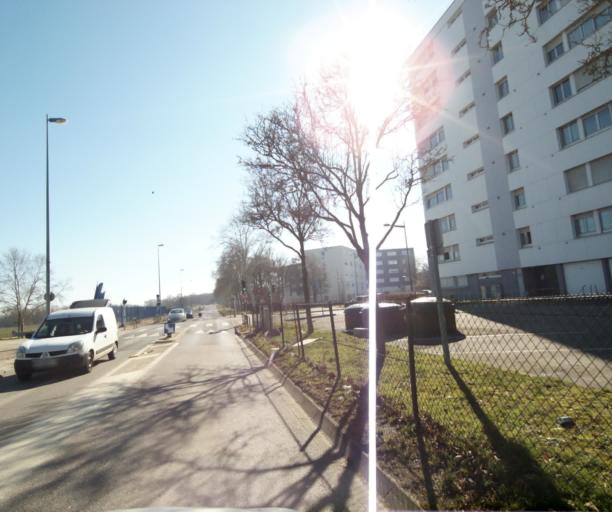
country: FR
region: Lorraine
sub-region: Departement de Meurthe-et-Moselle
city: Jarville-la-Malgrange
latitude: 48.6721
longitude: 6.2104
